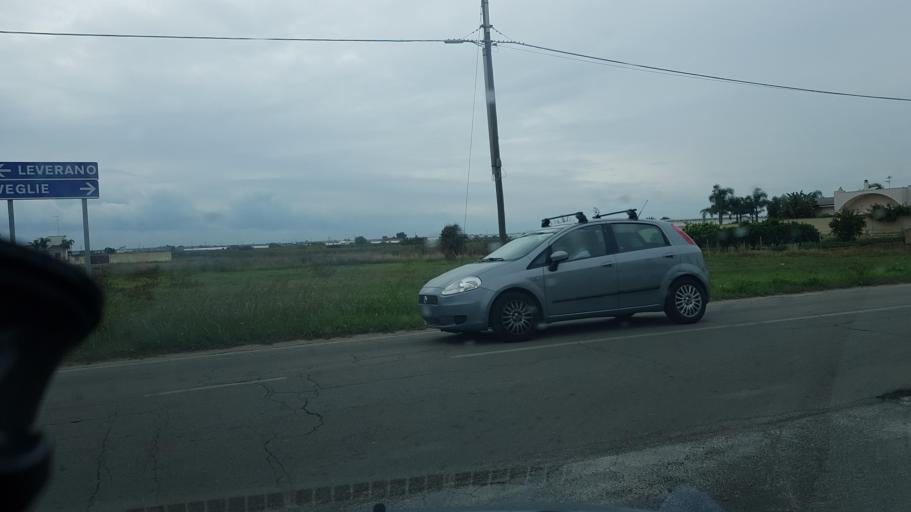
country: IT
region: Apulia
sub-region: Provincia di Lecce
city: Leverano
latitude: 40.3006
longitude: 17.9939
